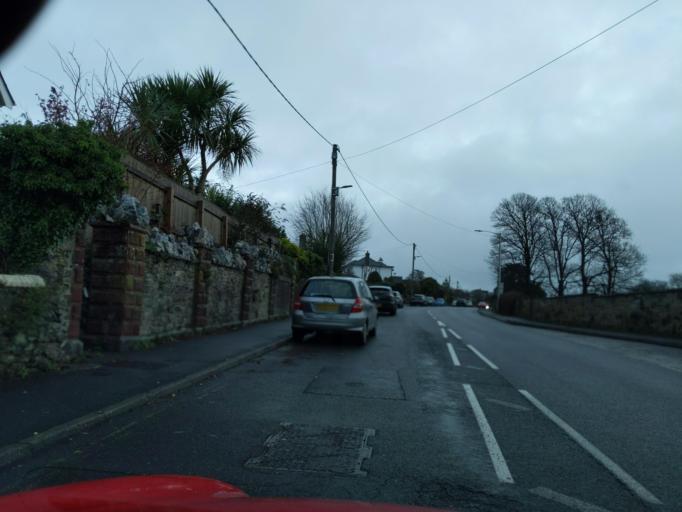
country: GB
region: England
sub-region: Devon
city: Plympton
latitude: 50.3871
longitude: -4.0463
